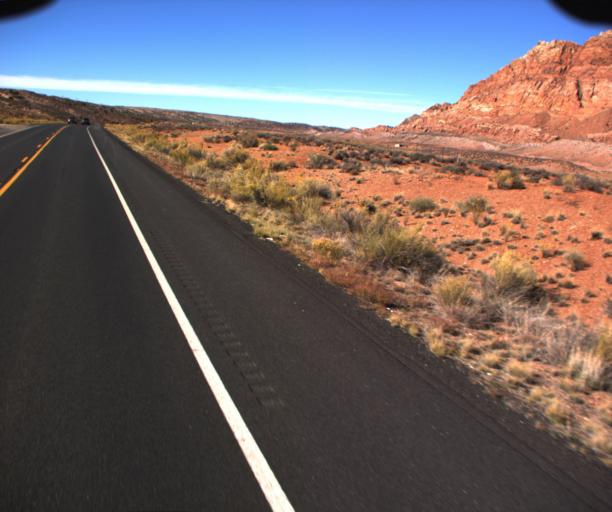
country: US
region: Arizona
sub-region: Coconino County
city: Tuba City
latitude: 36.3151
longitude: -111.4735
